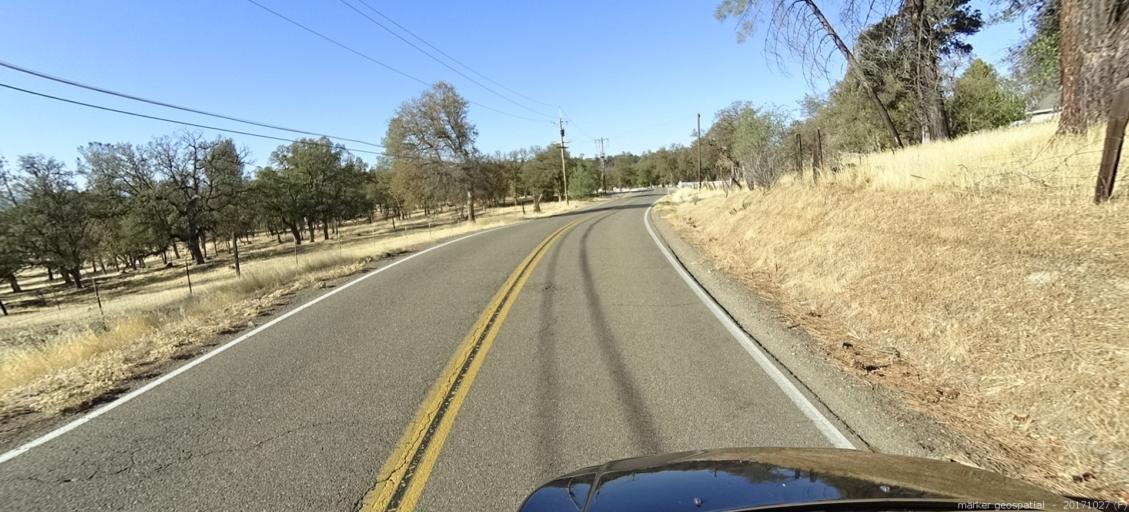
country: US
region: California
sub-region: Shasta County
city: Palo Cedro
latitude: 40.5595
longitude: -122.1885
